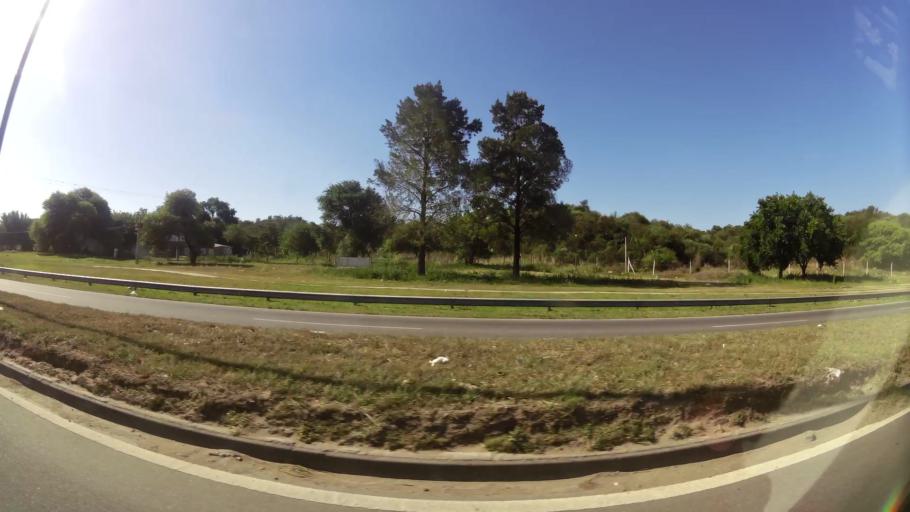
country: AR
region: Cordoba
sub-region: Departamento de Capital
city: Cordoba
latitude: -31.3985
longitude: -64.1371
